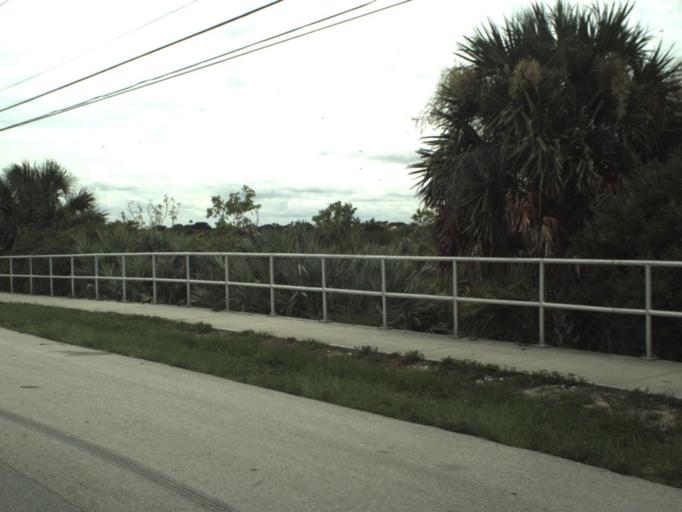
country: US
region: Florida
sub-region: Palm Beach County
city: Juno Beach
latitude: 26.8899
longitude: -80.0590
